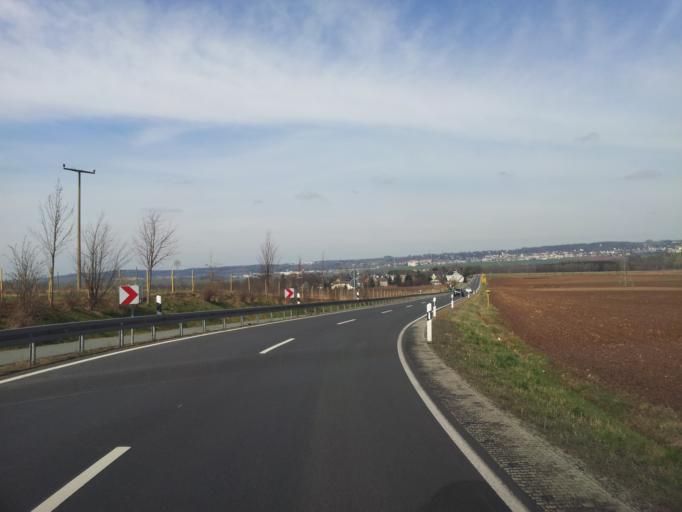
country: DE
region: Saxony
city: Gersdorf
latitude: 50.7536
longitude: 12.7204
